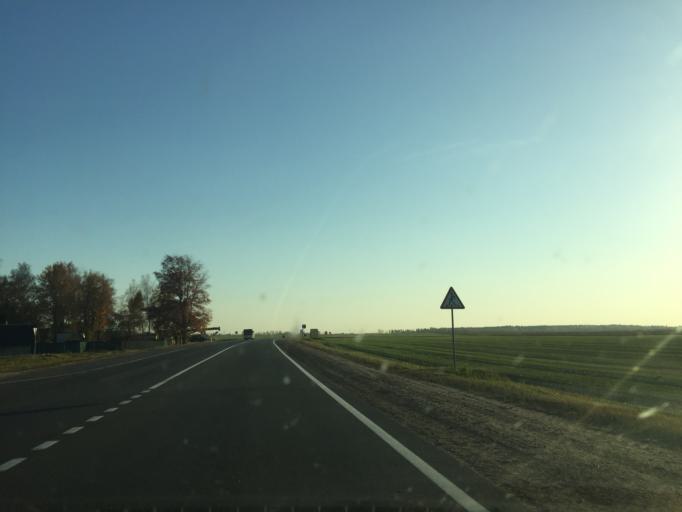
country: BY
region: Mogilev
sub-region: Mahilyowski Rayon
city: Kadino
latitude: 53.8800
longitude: 30.4882
